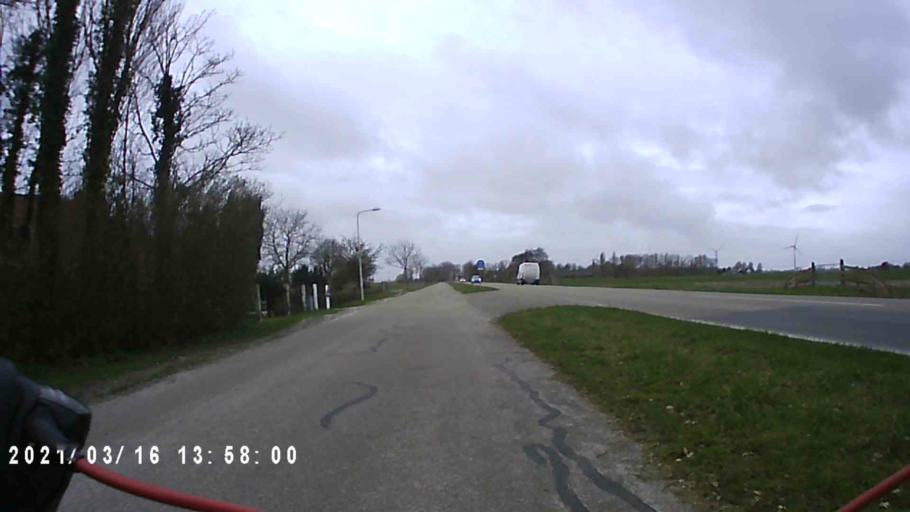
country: NL
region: Friesland
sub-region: Gemeente Franekeradeel
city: Franeker
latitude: 53.1838
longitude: 5.5043
